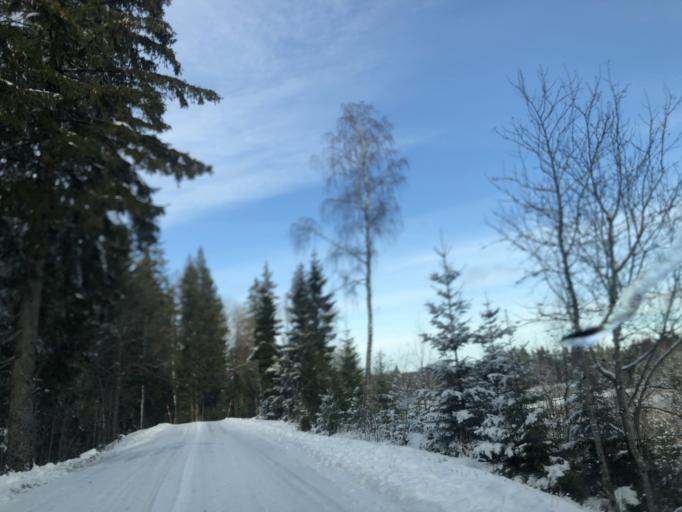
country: SE
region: Vaestra Goetaland
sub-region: Ulricehamns Kommun
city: Ulricehamn
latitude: 57.7675
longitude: 13.5203
